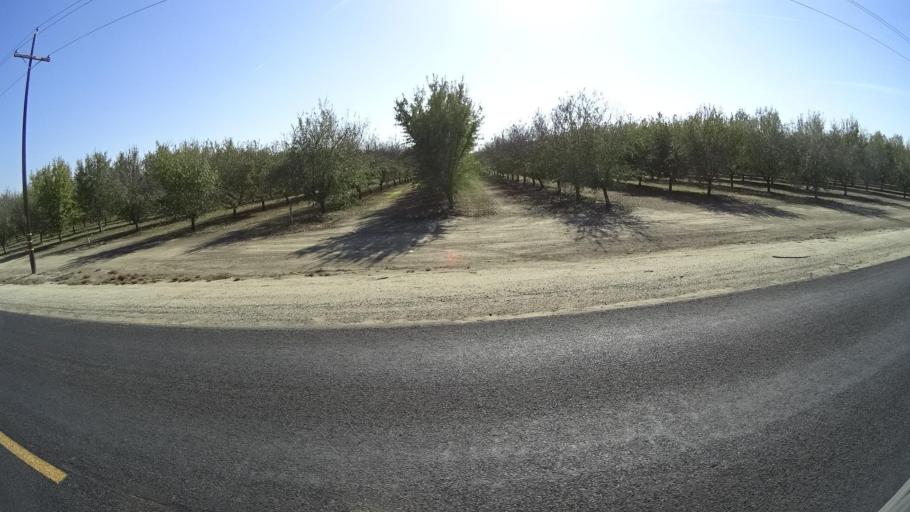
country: US
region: California
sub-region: Kern County
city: McFarland
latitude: 35.6454
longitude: -119.2492
